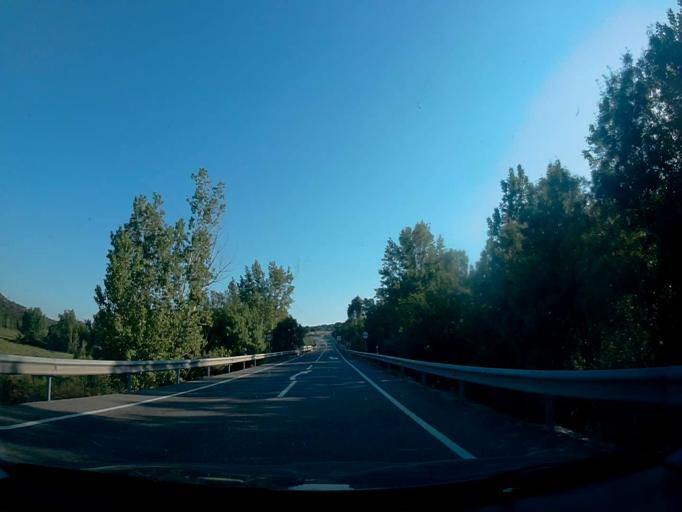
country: ES
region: Castille-La Mancha
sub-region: Province of Toledo
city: Escalona
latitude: 40.1930
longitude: -4.4025
